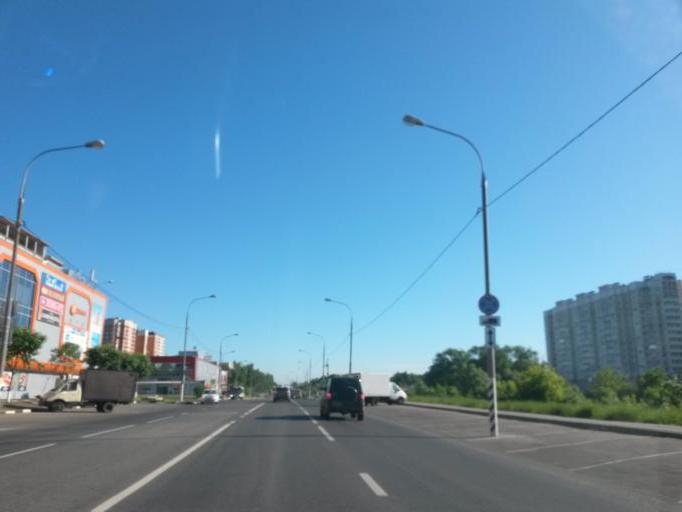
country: RU
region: Moskovskaya
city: Shcherbinka
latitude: 55.5027
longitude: 37.5729
